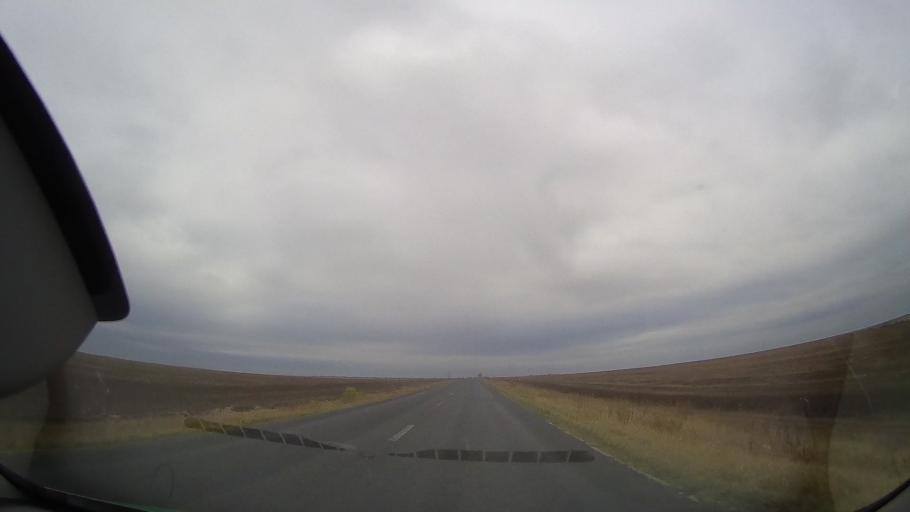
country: RO
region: Buzau
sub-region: Comuna Padina
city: Padina
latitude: 44.8128
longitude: 27.1252
